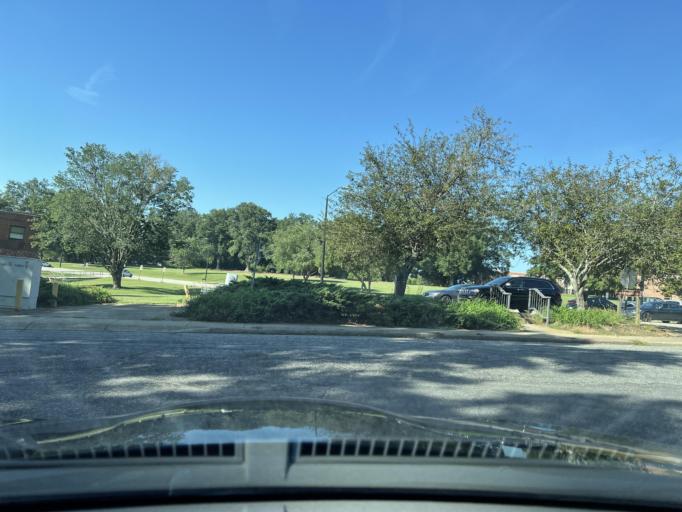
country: US
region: North Carolina
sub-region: Wake County
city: West Raleigh
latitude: 35.7723
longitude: -78.6639
